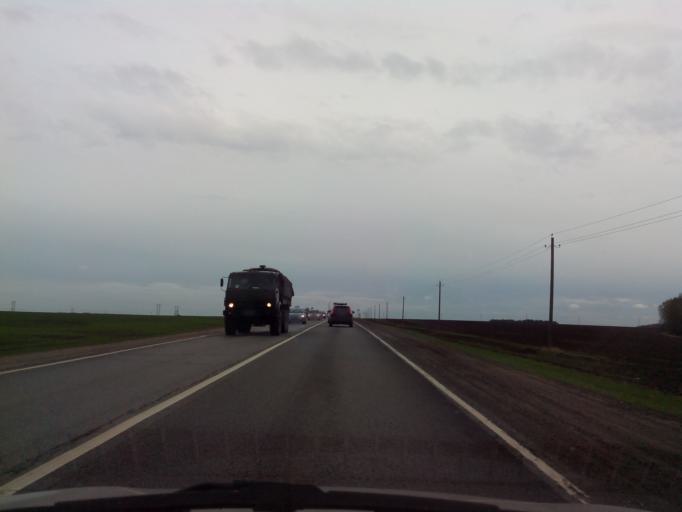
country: RU
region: Moskovskaya
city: Ozherel'ye
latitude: 54.7073
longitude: 38.2964
